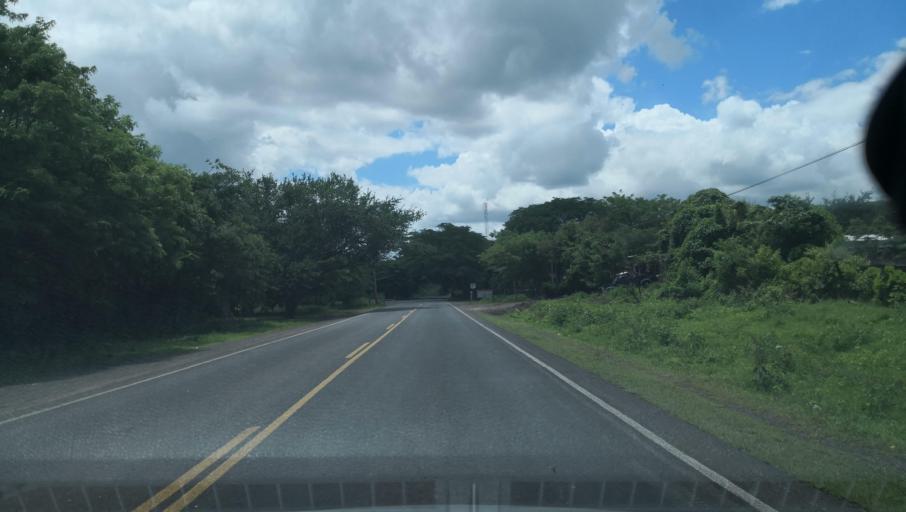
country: NI
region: Esteli
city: Condega
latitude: 13.4053
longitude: -86.4002
